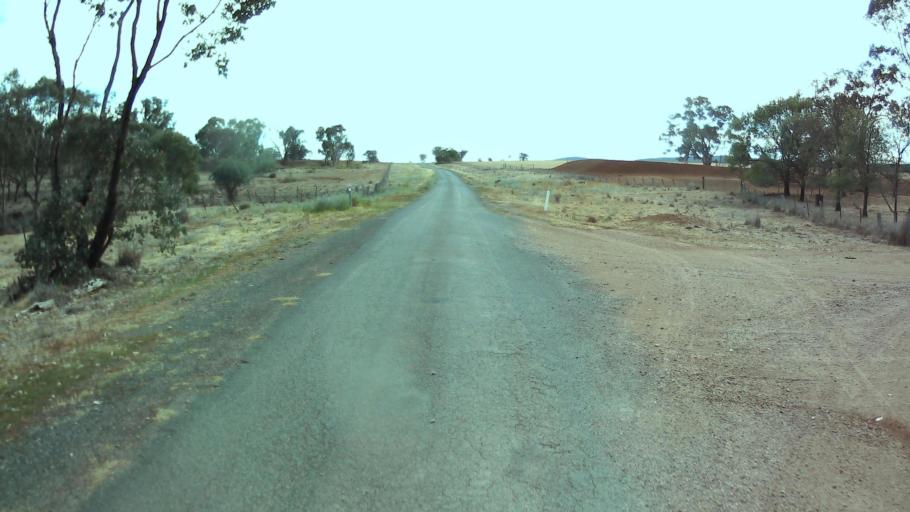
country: AU
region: New South Wales
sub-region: Weddin
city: Grenfell
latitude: -33.8389
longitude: 148.2655
